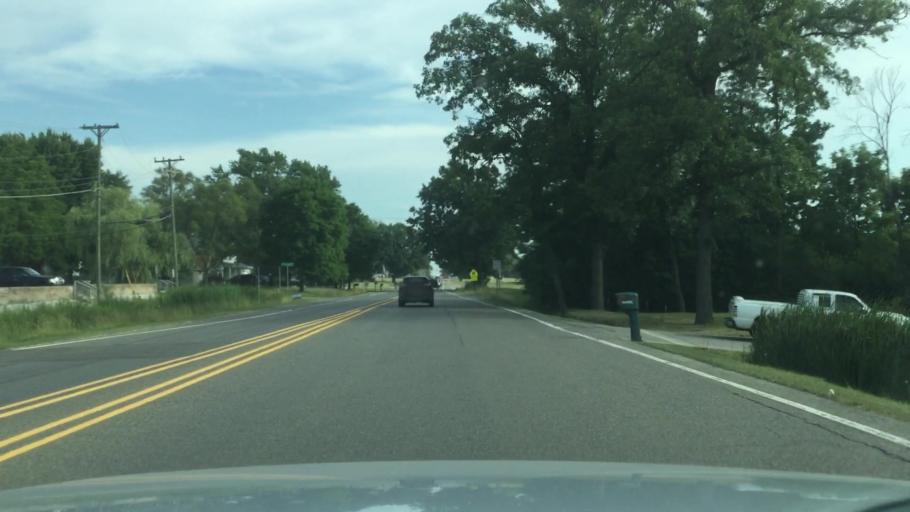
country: US
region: Michigan
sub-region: Oakland County
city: Sylvan Lake
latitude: 42.6600
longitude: -83.3468
